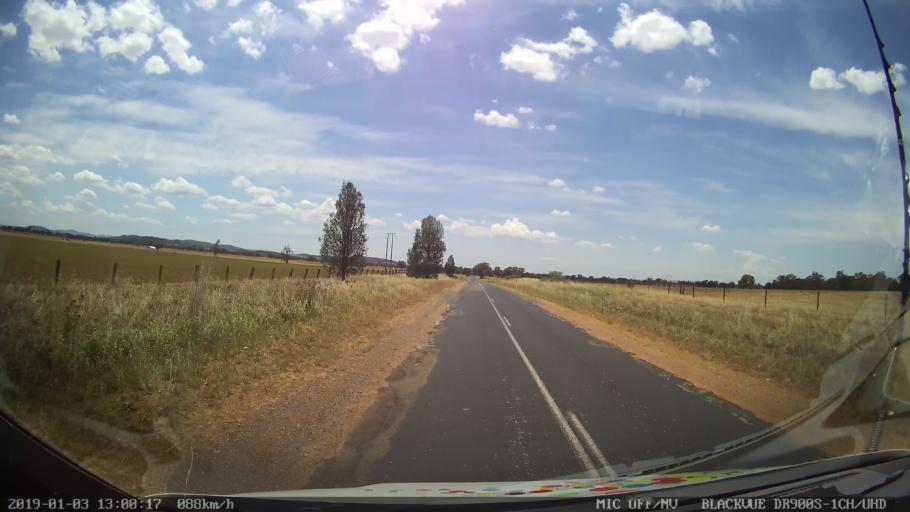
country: AU
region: New South Wales
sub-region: Cabonne
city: Canowindra
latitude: -33.6318
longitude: 148.4012
